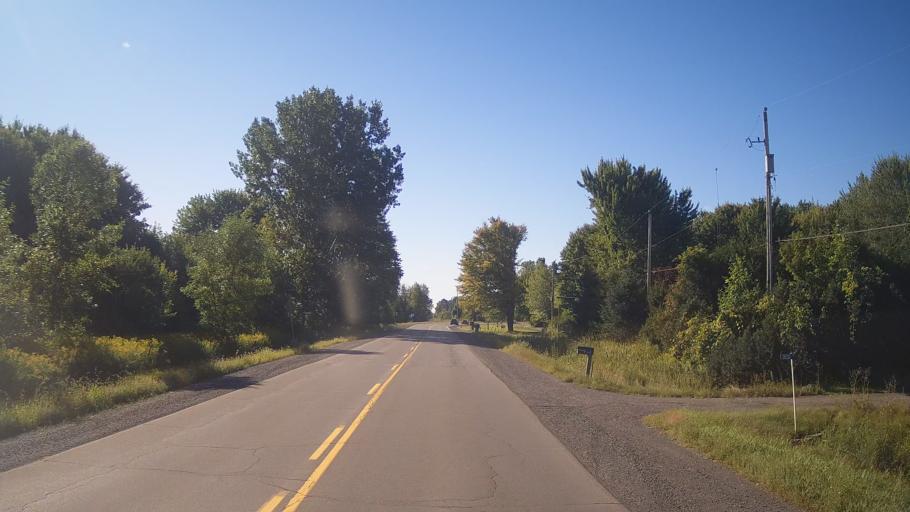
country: CA
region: Ontario
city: Bells Corners
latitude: 45.1081
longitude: -75.6149
